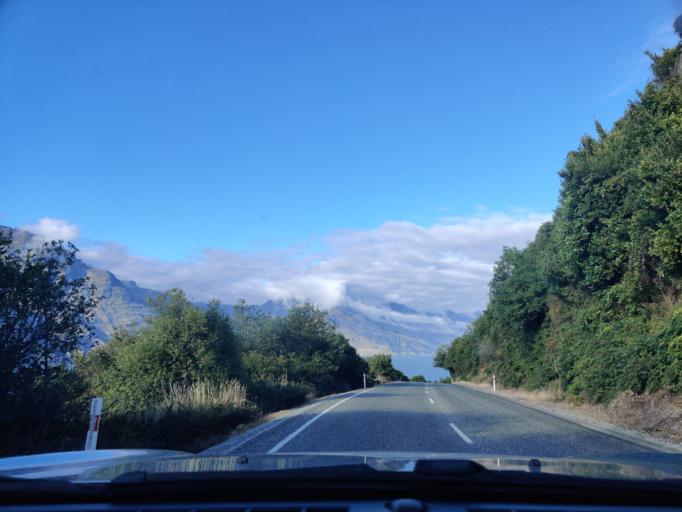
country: NZ
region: Otago
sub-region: Queenstown-Lakes District
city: Queenstown
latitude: -45.0544
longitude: 168.6153
